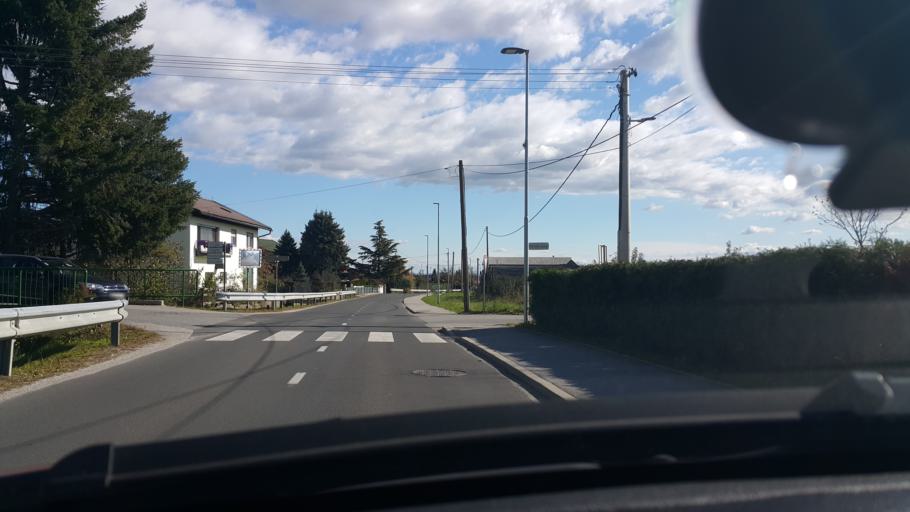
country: SI
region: Race-Fram
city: Fram
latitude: 46.4535
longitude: 15.6386
